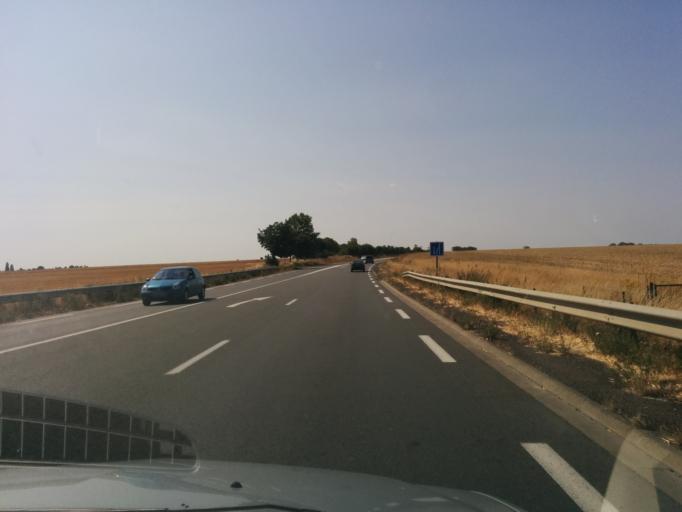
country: FR
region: Poitou-Charentes
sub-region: Departement de la Vienne
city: Neuville-de-Poitou
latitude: 46.7002
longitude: 0.2408
